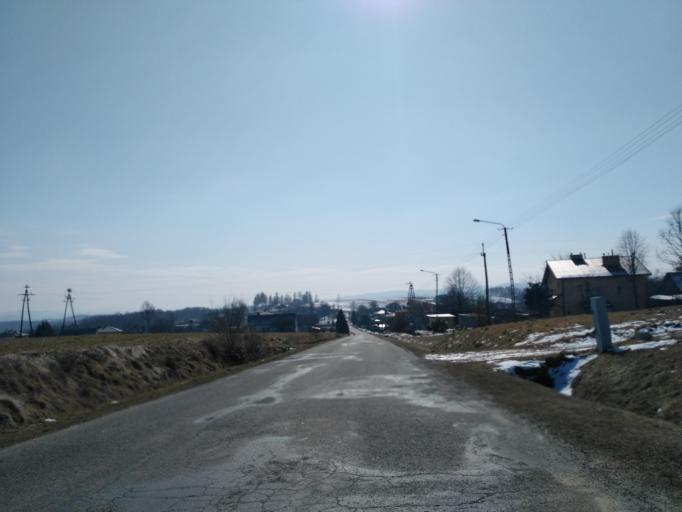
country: PL
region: Subcarpathian Voivodeship
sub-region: Powiat brzozowski
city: Jasienica Rosielna
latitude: 49.7654
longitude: 21.9264
